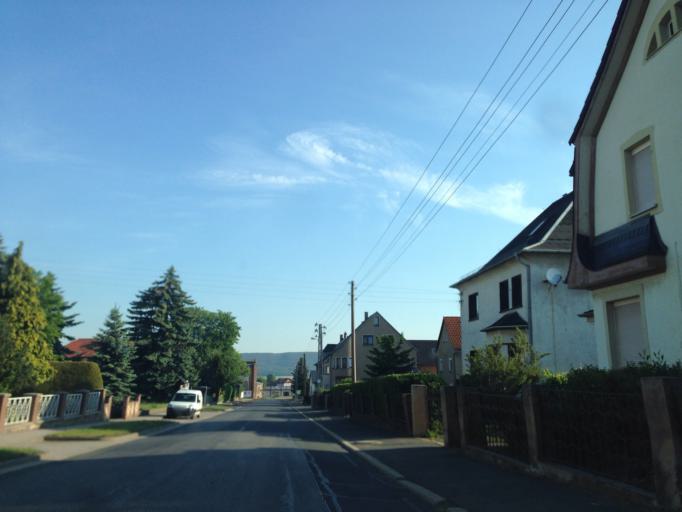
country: DE
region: Thuringia
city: Konitz
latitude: 50.6568
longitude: 11.4911
